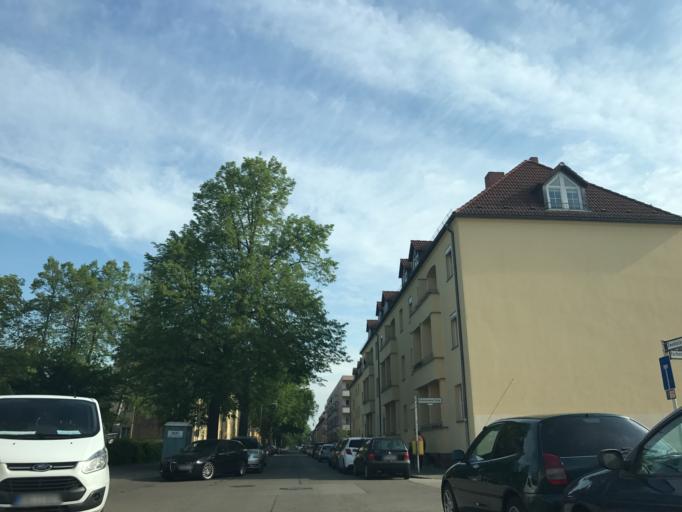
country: DE
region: Berlin
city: Spandau
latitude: 52.5441
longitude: 13.1882
